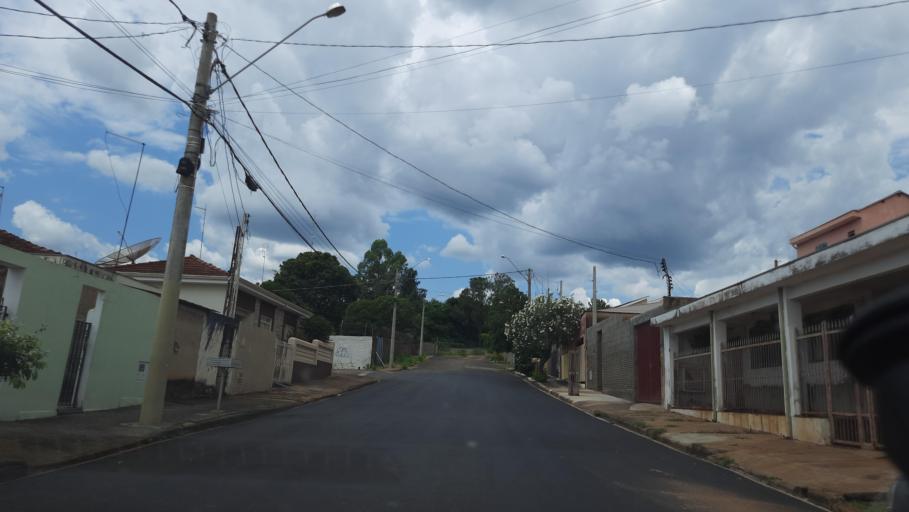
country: BR
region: Sao Paulo
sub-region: Cajuru
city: Cajuru
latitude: -21.2747
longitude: -47.2991
